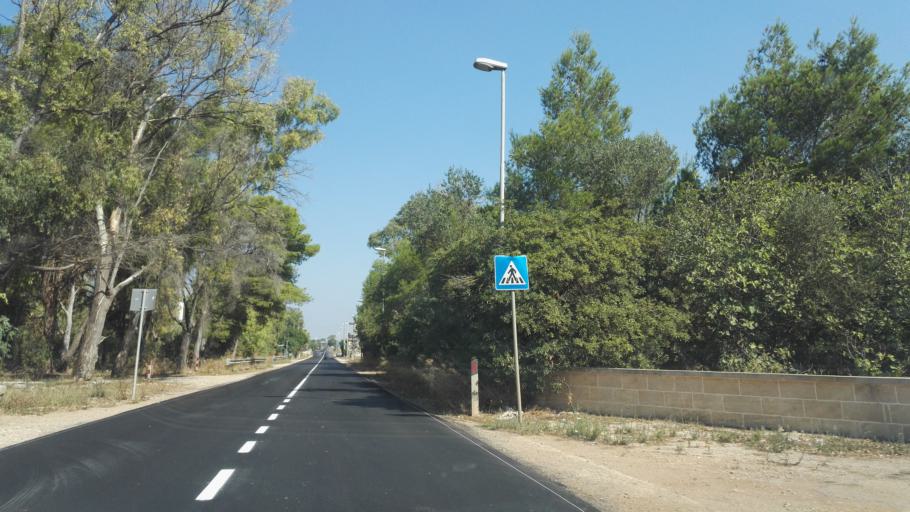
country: IT
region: Apulia
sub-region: Provincia di Lecce
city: Nardo
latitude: 40.2010
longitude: 17.9585
